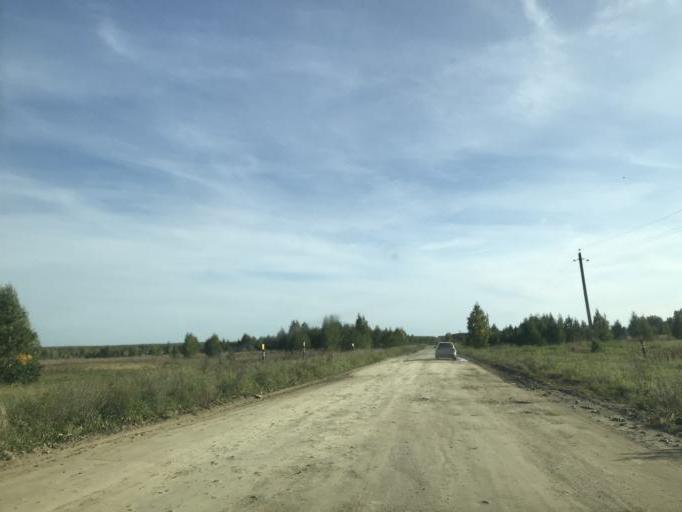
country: RU
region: Chelyabinsk
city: Poletayevo
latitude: 54.9771
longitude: 60.9695
